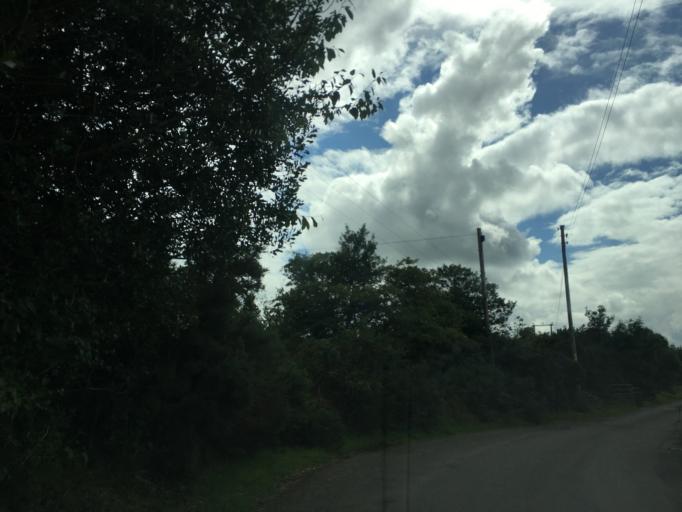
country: GB
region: Scotland
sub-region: Argyll and Bute
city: Oban
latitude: 56.4377
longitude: -5.2315
